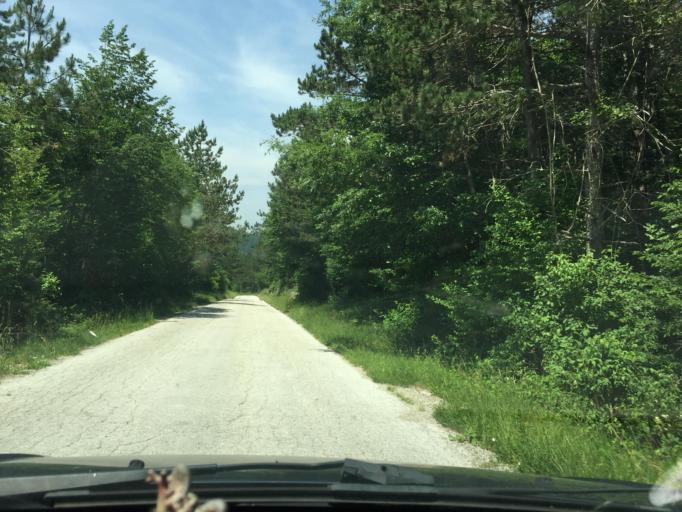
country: HR
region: Istarska
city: Buzet
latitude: 45.4793
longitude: 14.0619
